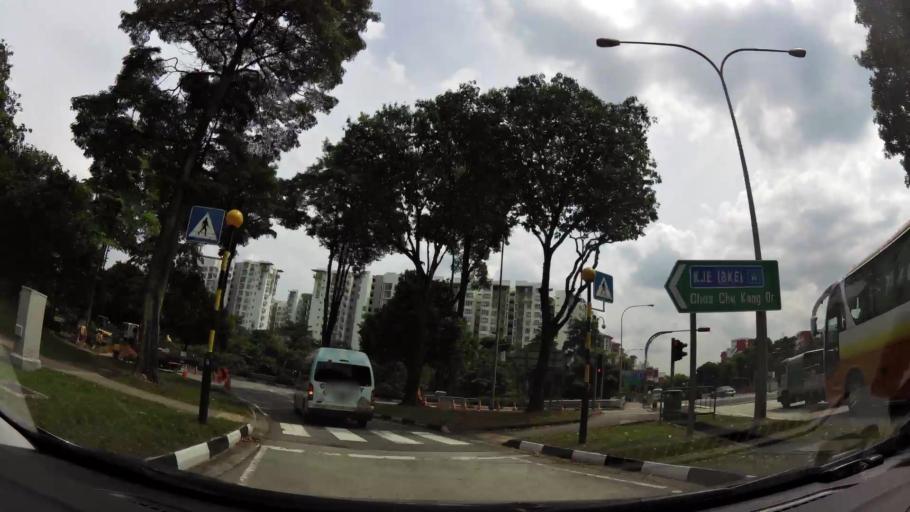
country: MY
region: Johor
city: Johor Bahru
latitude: 1.3874
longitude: 103.7414
